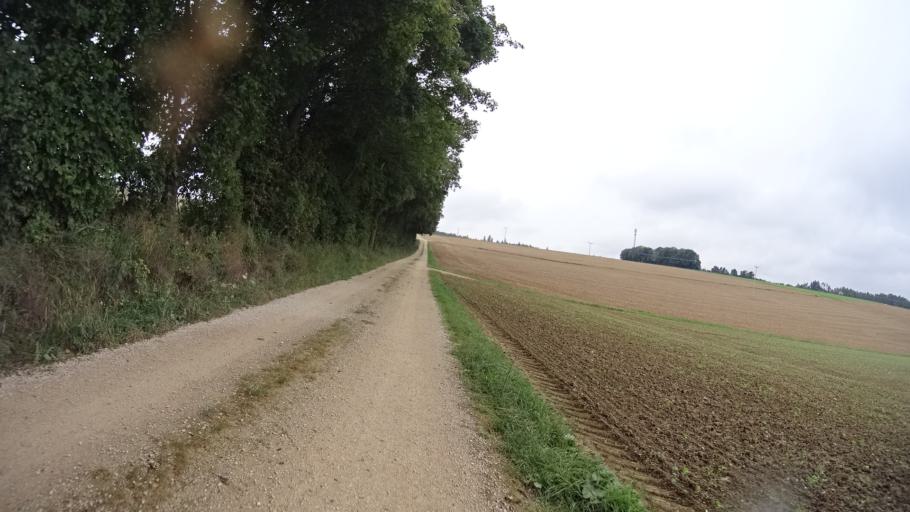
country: DE
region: Bavaria
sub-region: Upper Bavaria
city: Bohmfeld
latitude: 48.8554
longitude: 11.3575
